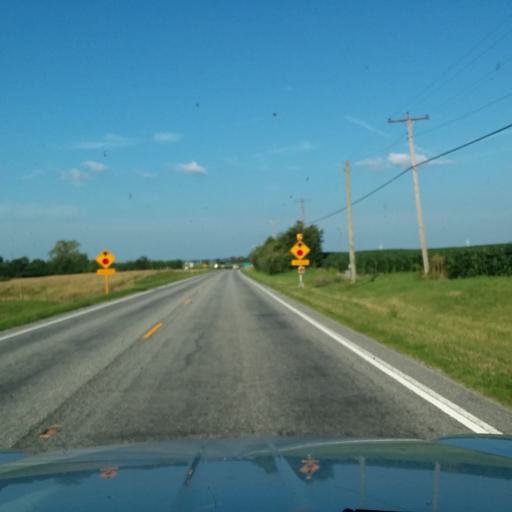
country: US
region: Indiana
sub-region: Johnson County
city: Princes Lakes
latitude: 39.4100
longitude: -86.0901
